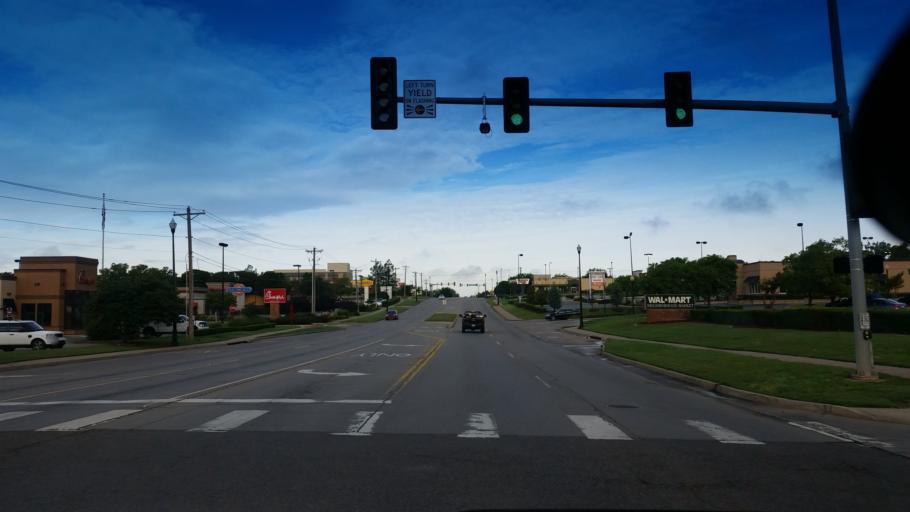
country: US
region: Oklahoma
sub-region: Oklahoma County
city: Edmond
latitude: 35.6528
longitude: -97.4630
